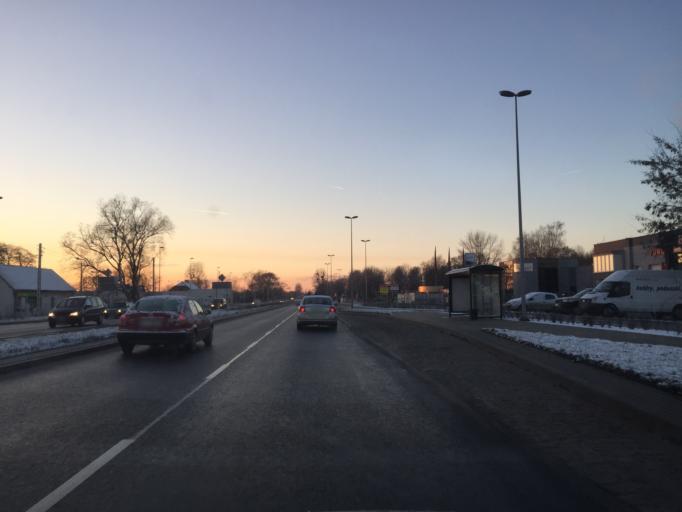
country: PL
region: Kujawsko-Pomorskie
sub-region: Powiat torunski
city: Lubicz Dolny
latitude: 53.0371
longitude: 18.6738
